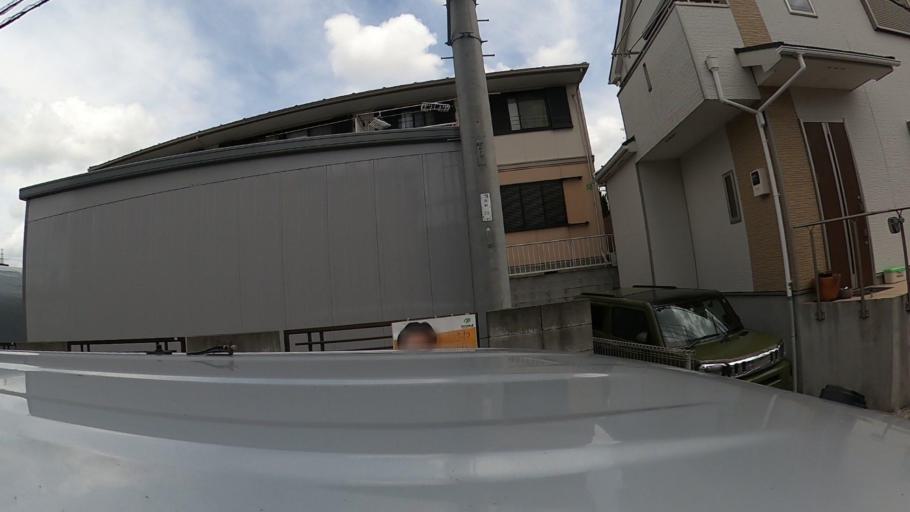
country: JP
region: Kanagawa
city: Minami-rinkan
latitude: 35.4168
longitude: 139.4749
